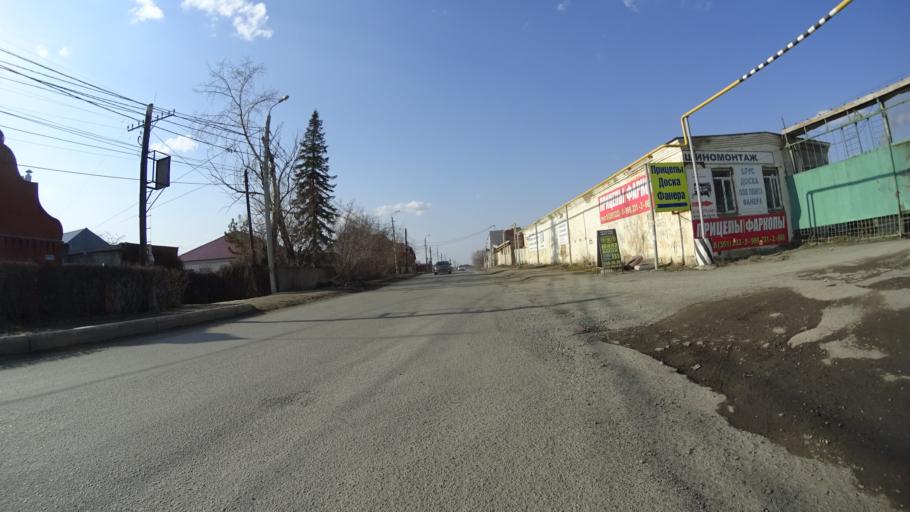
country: RU
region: Chelyabinsk
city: Novosineglazovskiy
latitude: 55.1080
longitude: 61.3349
